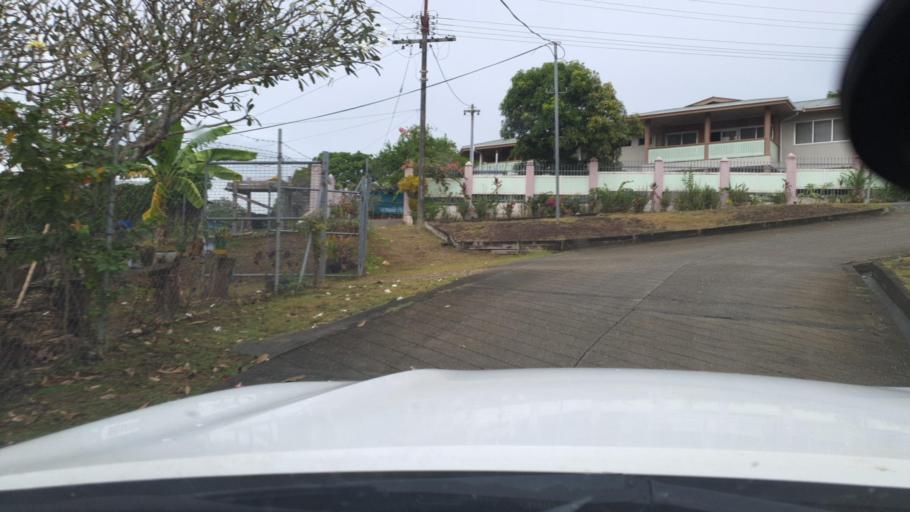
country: SB
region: Guadalcanal
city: Honiara
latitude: -9.4397
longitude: 159.9811
